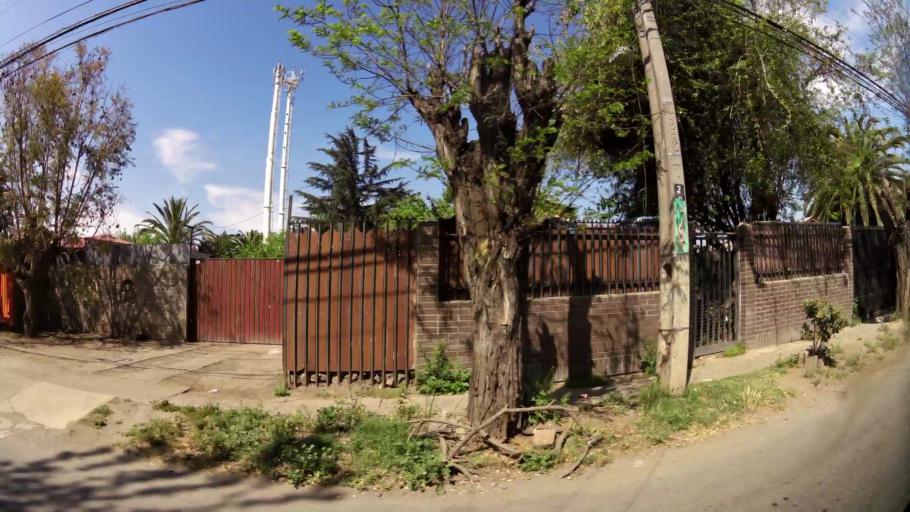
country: CL
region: Santiago Metropolitan
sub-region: Provincia de Santiago
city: Lo Prado
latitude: -33.4041
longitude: -70.7171
